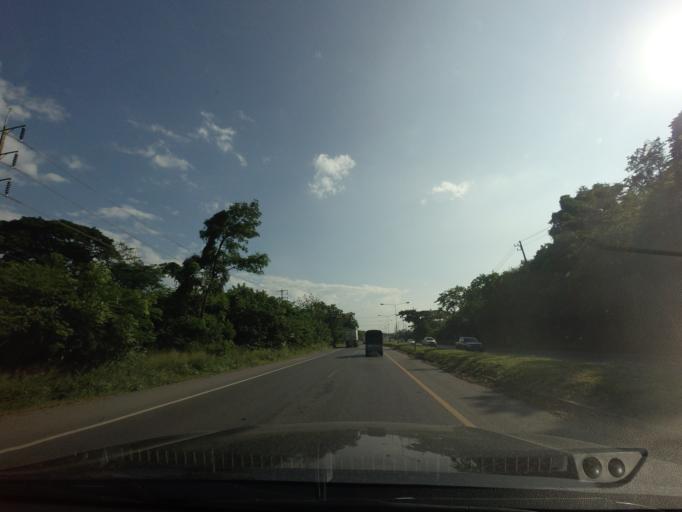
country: TH
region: Sara Buri
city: Phra Phutthabat
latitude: 14.7258
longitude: 100.9056
